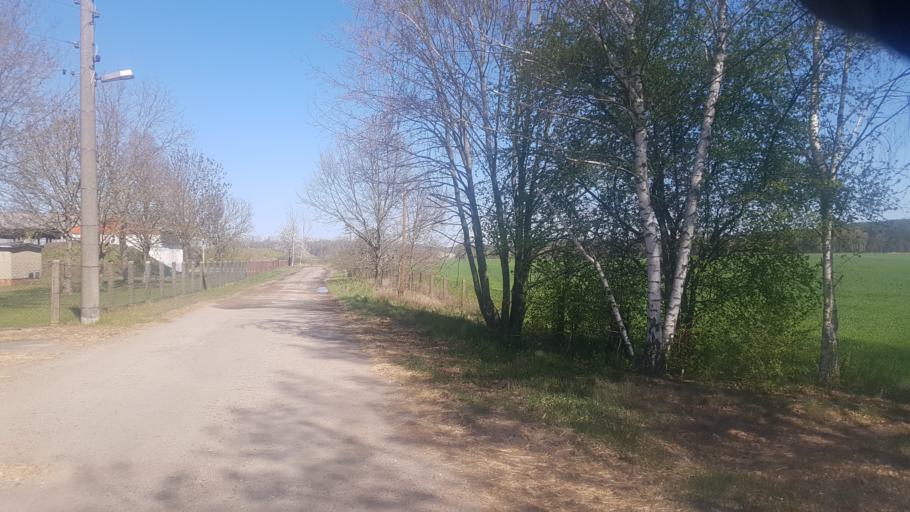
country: DE
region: Brandenburg
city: Sonnewalde
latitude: 51.7195
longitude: 13.6508
